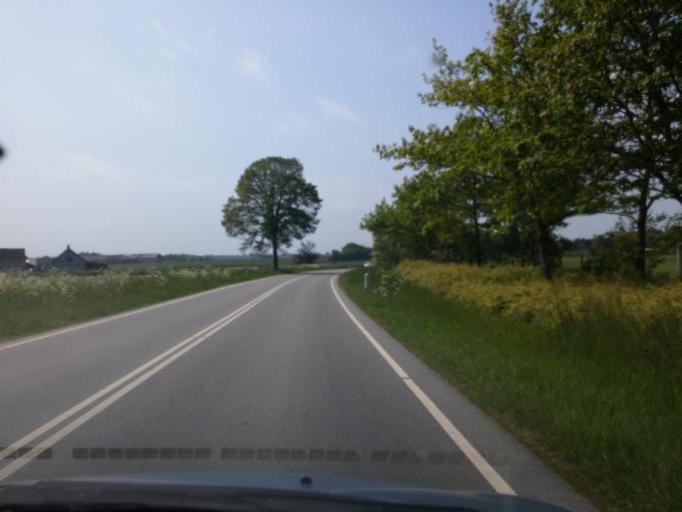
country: DK
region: South Denmark
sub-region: Kerteminde Kommune
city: Langeskov
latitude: 55.4086
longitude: 10.5951
